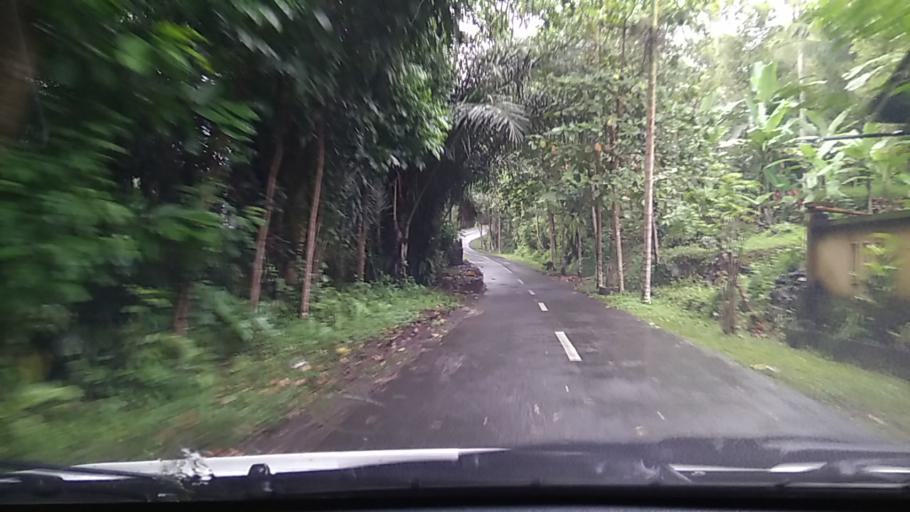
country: ID
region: Bali
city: Tiyingtali Kelod
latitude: -8.4102
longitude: 115.6238
